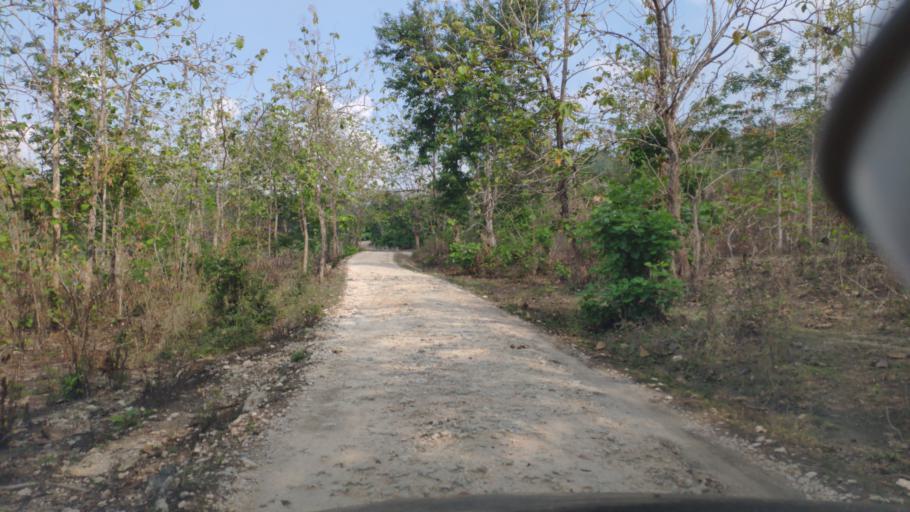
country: ID
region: Central Java
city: Semanggi
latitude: -7.0563
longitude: 111.4178
